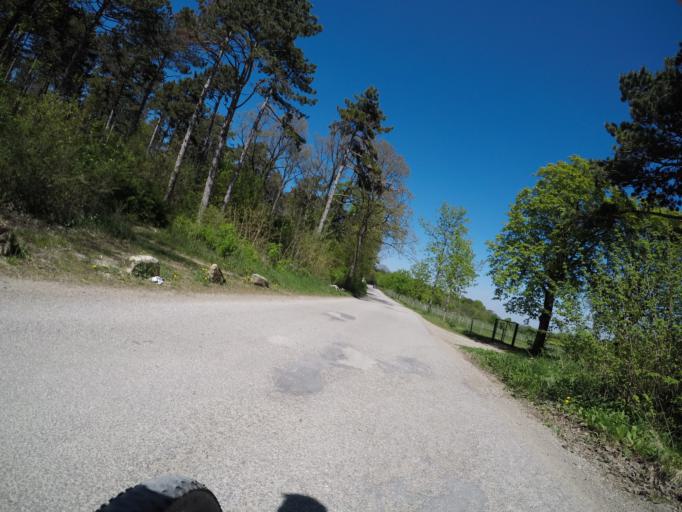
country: AT
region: Lower Austria
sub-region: Politischer Bezirk Modling
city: Gumpoldskirchen
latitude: 48.0575
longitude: 16.2761
